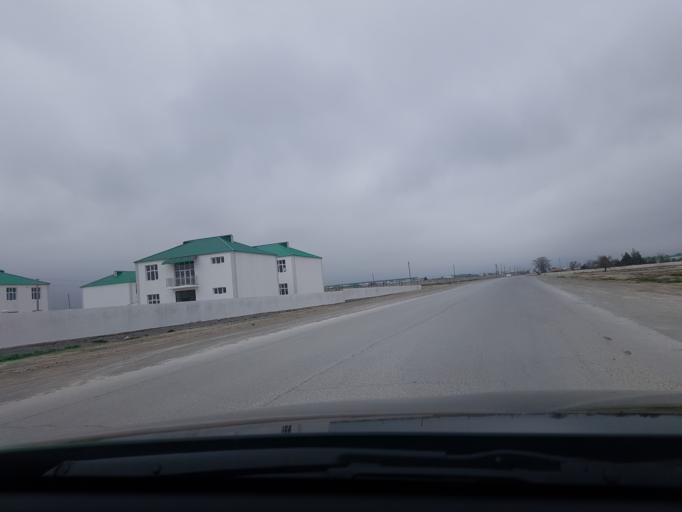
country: TM
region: Ahal
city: Abadan
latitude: 38.1361
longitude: 57.9482
